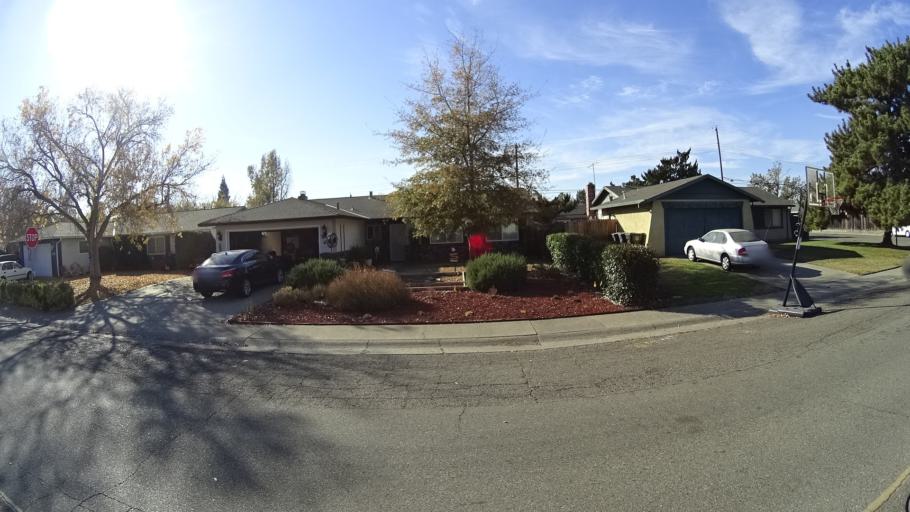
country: US
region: California
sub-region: Sacramento County
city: Antelope
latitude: 38.7040
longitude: -121.3208
